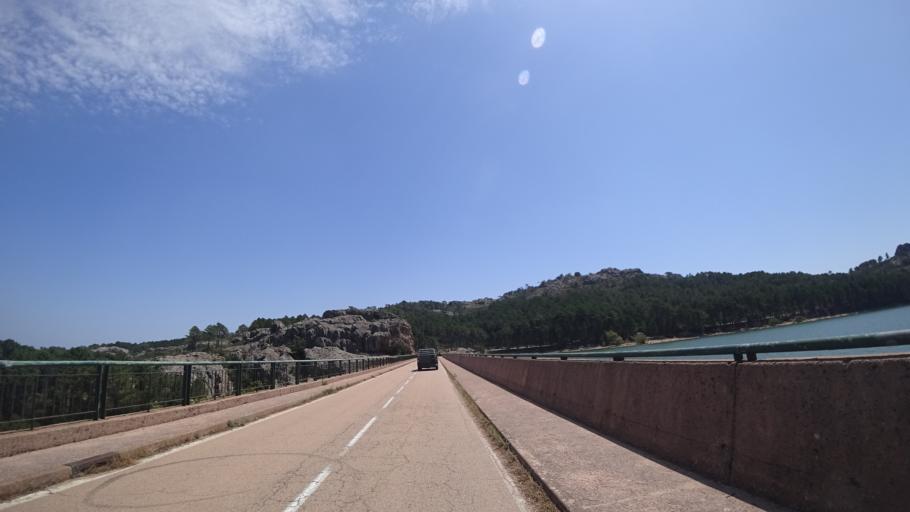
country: FR
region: Corsica
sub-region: Departement de la Corse-du-Sud
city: Zonza
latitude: 41.6688
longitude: 9.2069
